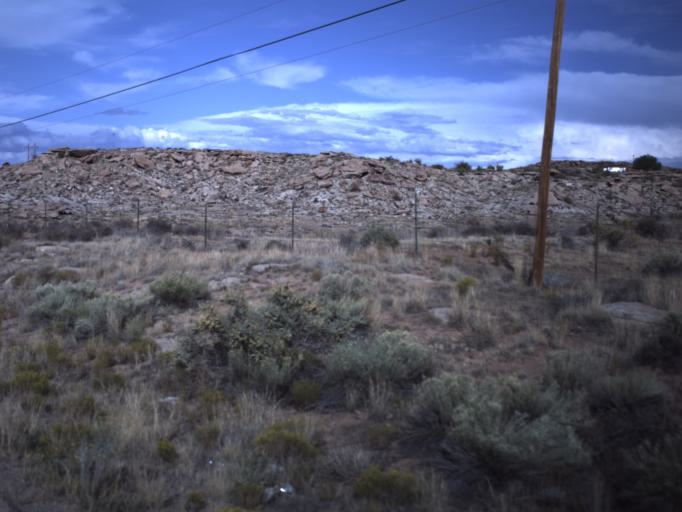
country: US
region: Utah
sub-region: San Juan County
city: Blanding
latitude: 37.2781
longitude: -109.2959
